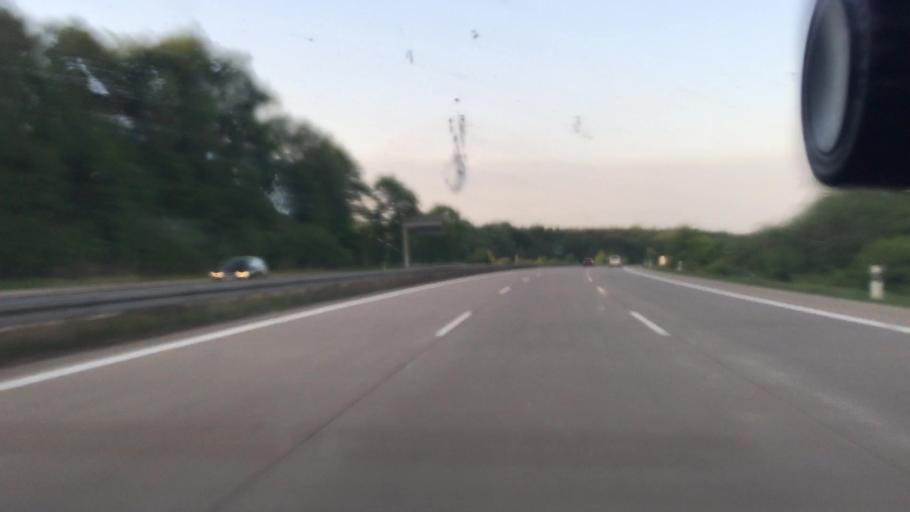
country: DE
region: Saxony
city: Hainichen
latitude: 50.9869
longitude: 13.1009
